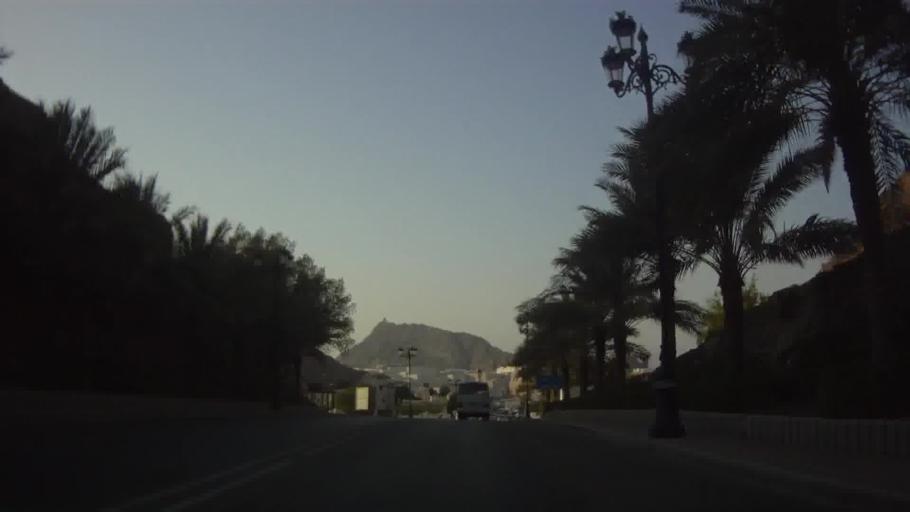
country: OM
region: Muhafazat Masqat
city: Muscat
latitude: 23.6079
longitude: 58.5964
